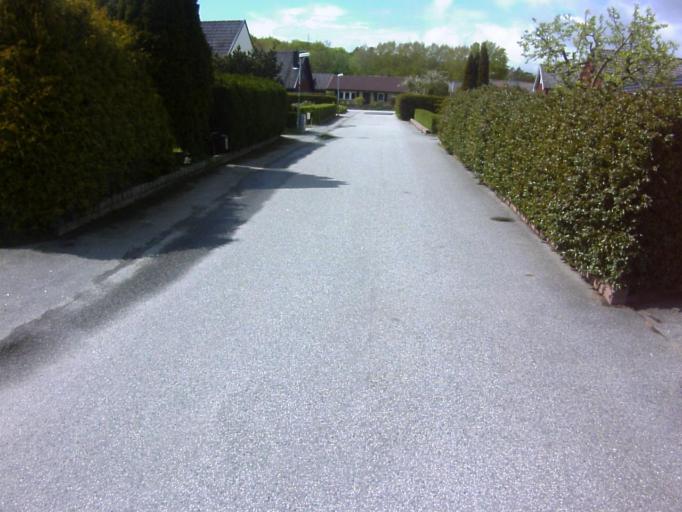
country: SE
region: Blekinge
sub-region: Solvesborgs Kommun
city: Soelvesborg
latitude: 56.0629
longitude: 14.5824
